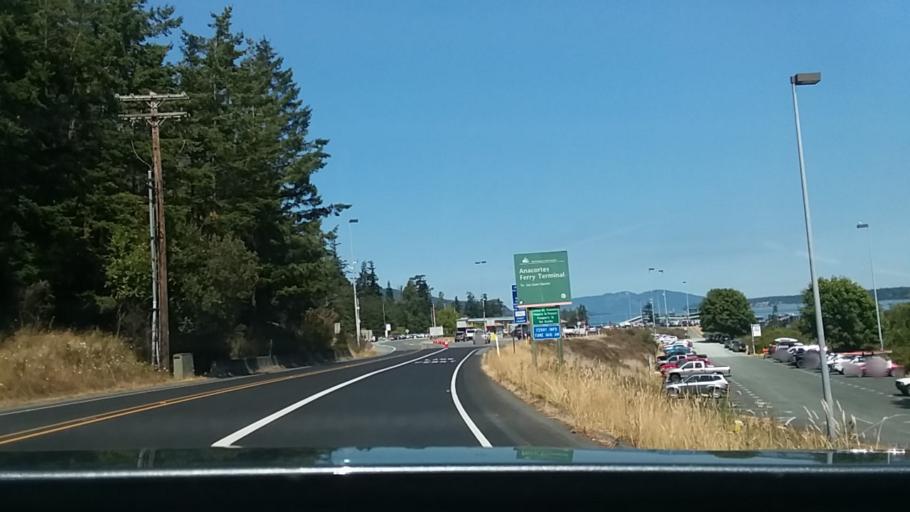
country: US
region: Washington
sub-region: Skagit County
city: Anacortes
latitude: 48.5018
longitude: -122.6793
